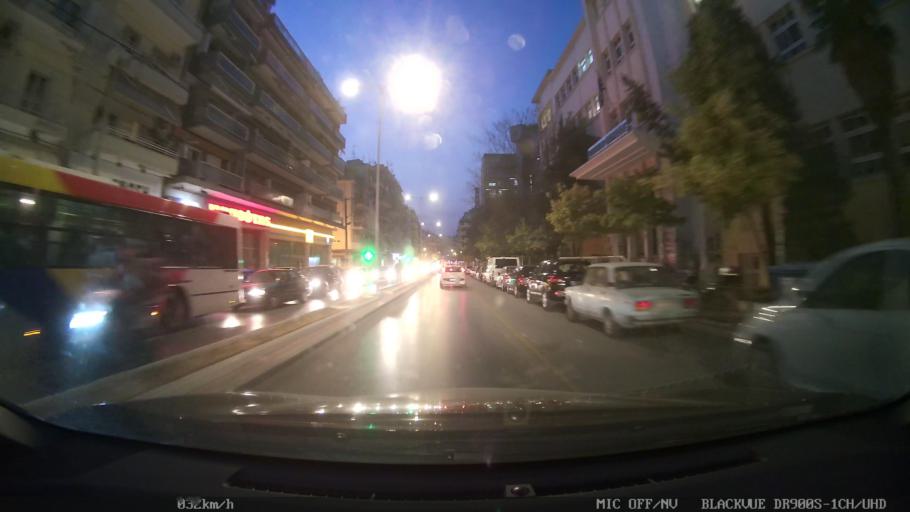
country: GR
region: Central Macedonia
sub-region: Nomos Thessalonikis
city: Triandria
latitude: 40.6167
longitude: 22.9607
